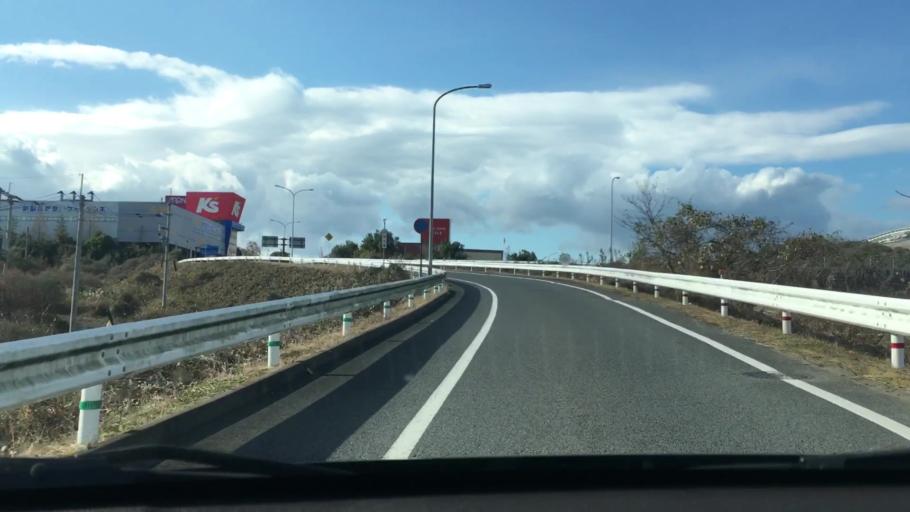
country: JP
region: Oita
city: Tsurusaki
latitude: 33.1952
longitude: 131.6635
